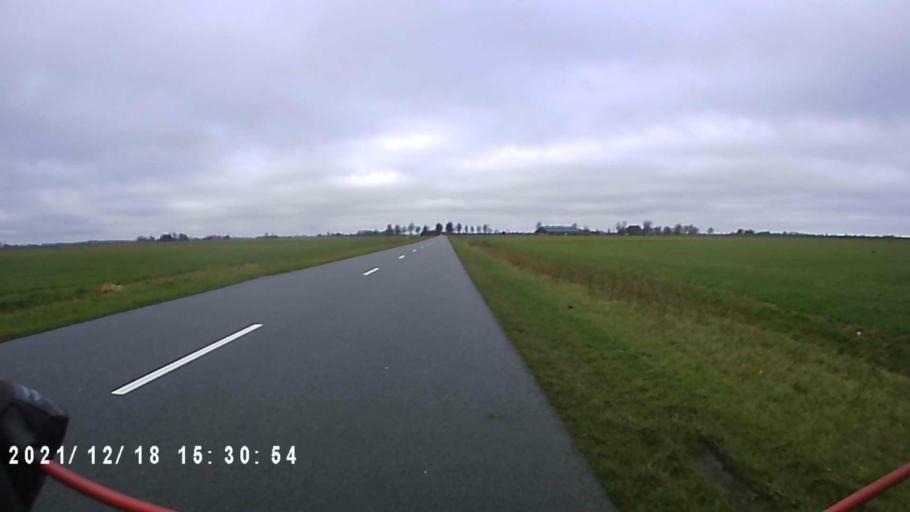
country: NL
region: Friesland
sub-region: Gemeente Dongeradeel
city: Anjum
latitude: 53.3378
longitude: 6.1381
